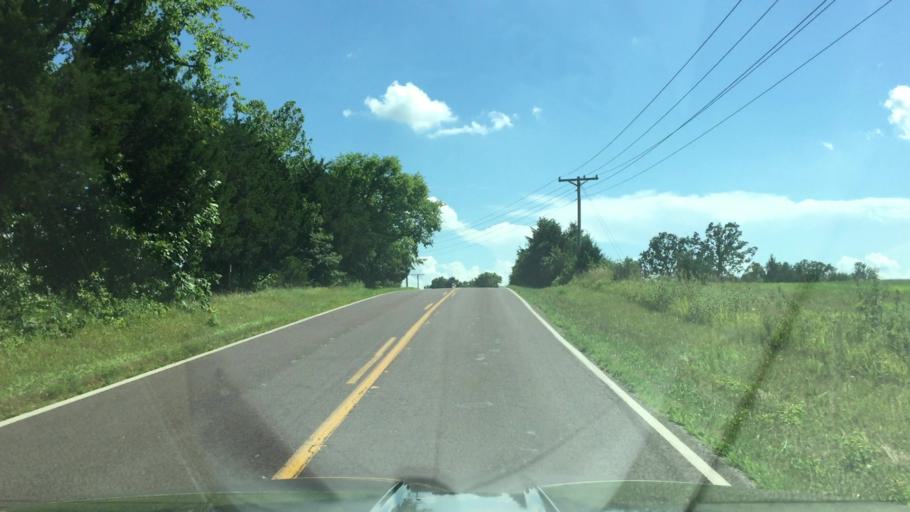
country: US
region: Missouri
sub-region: Miller County
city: Tuscumbia
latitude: 38.1216
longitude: -92.4686
